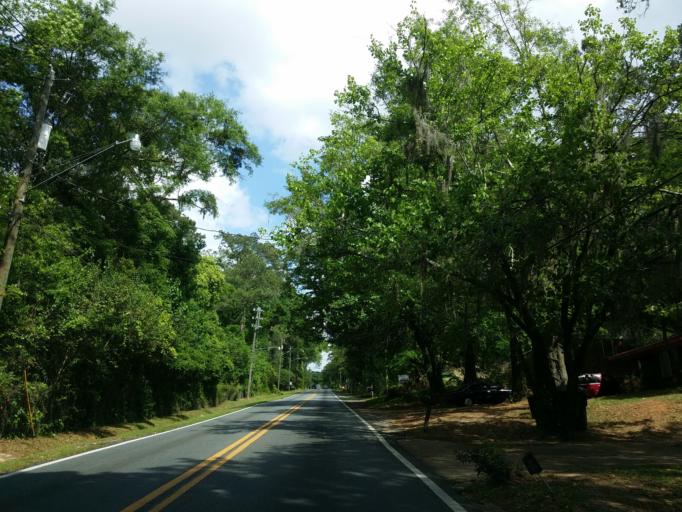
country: US
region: Florida
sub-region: Leon County
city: Tallahassee
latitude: 30.4200
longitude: -84.2711
